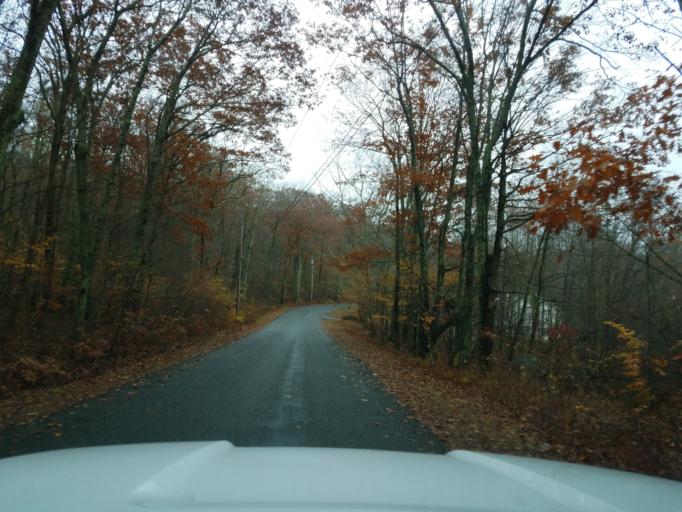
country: US
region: Connecticut
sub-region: Windham County
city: Windham
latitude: 41.7897
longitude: -72.1050
